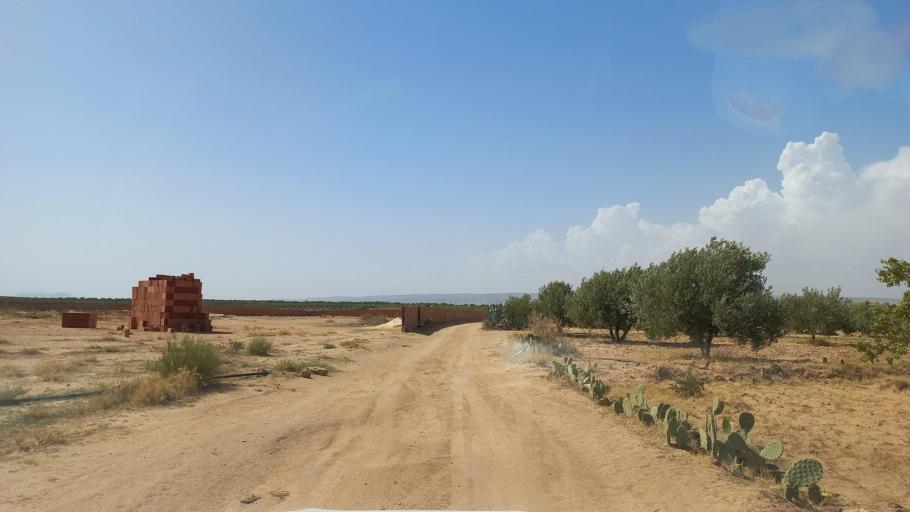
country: TN
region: Al Qasrayn
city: Kasserine
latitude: 35.2097
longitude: 9.0385
